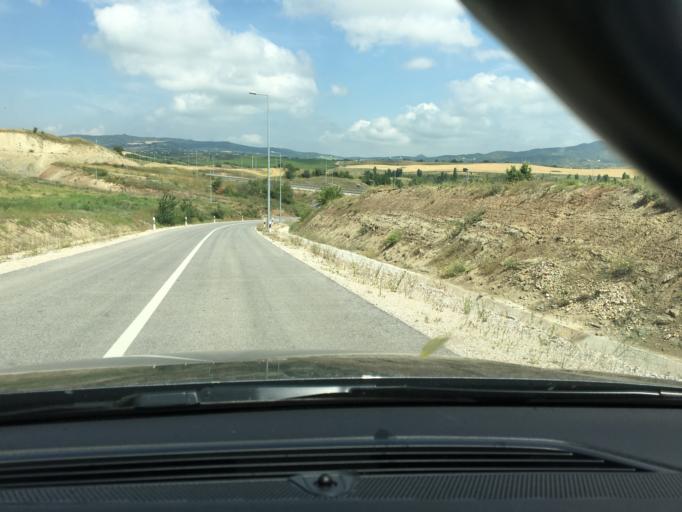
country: MK
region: Sveti Nikole
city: Gorobinci
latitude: 41.9151
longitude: 21.8794
